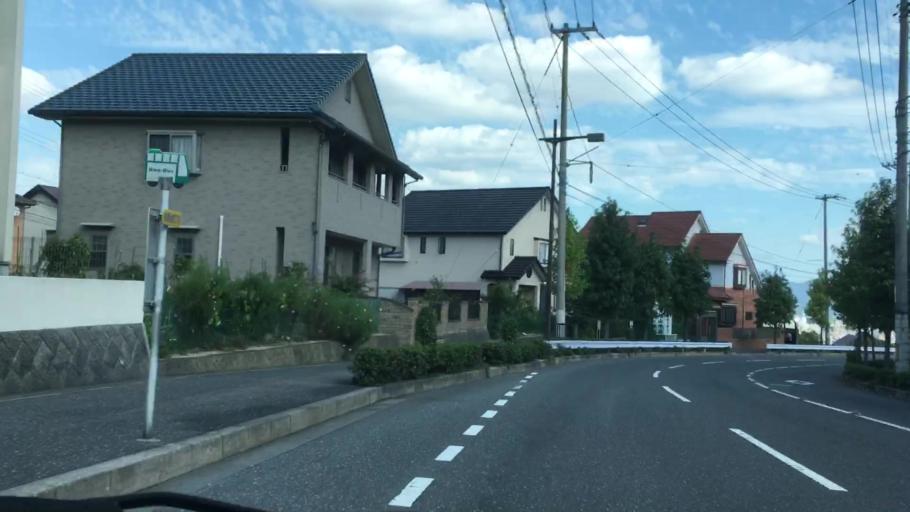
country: JP
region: Hiroshima
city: Hiroshima-shi
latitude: 34.4011
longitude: 132.4166
